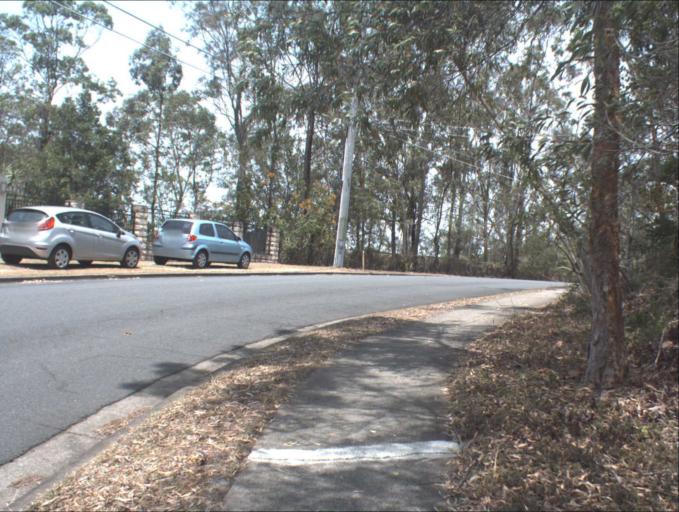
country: AU
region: Queensland
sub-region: Logan
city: Beenleigh
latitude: -27.6642
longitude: 153.1996
